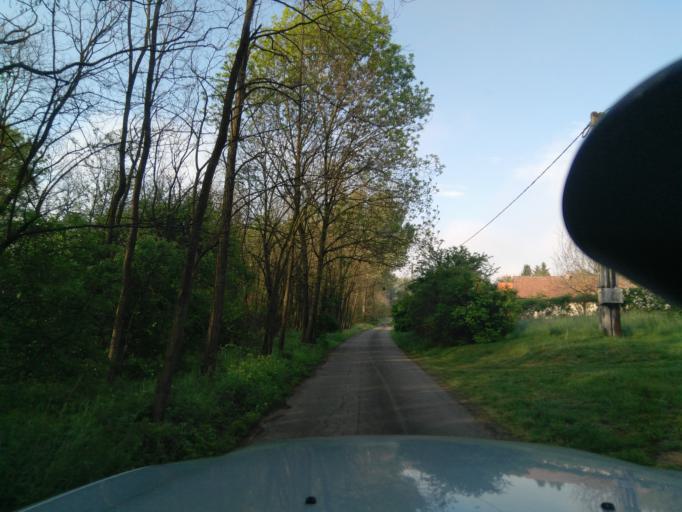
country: HU
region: Zala
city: Sarmellek
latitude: 46.7421
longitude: 17.1423
